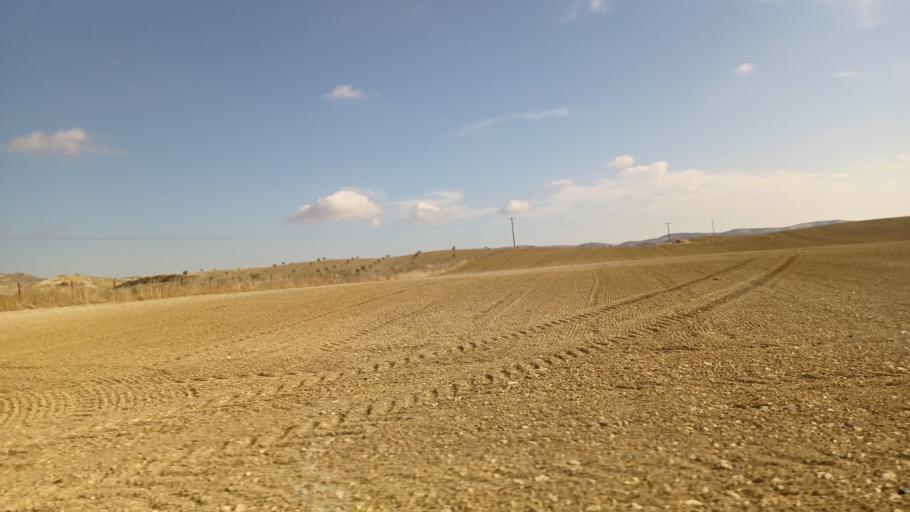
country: CY
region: Larnaka
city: Troulloi
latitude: 35.0261
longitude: 33.5824
